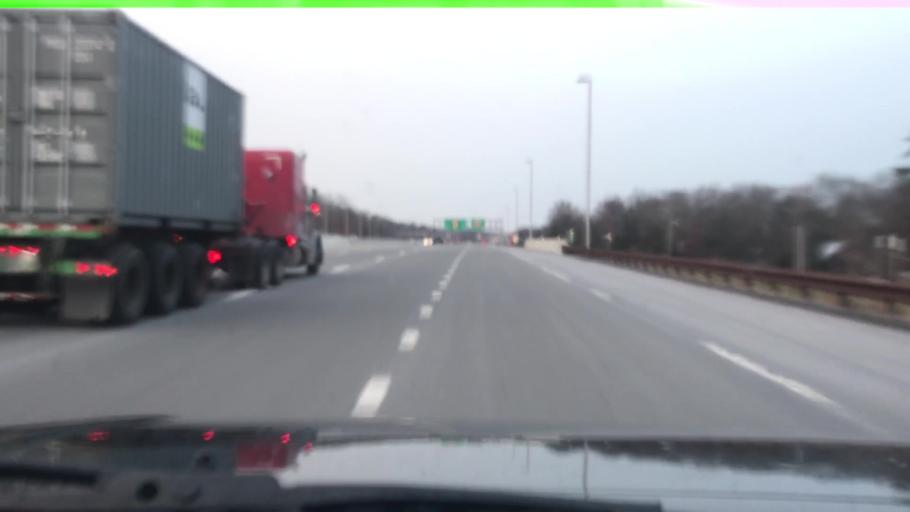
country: US
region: New Jersey
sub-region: Ocean County
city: Silver Ridge
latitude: 39.9916
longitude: -74.2091
